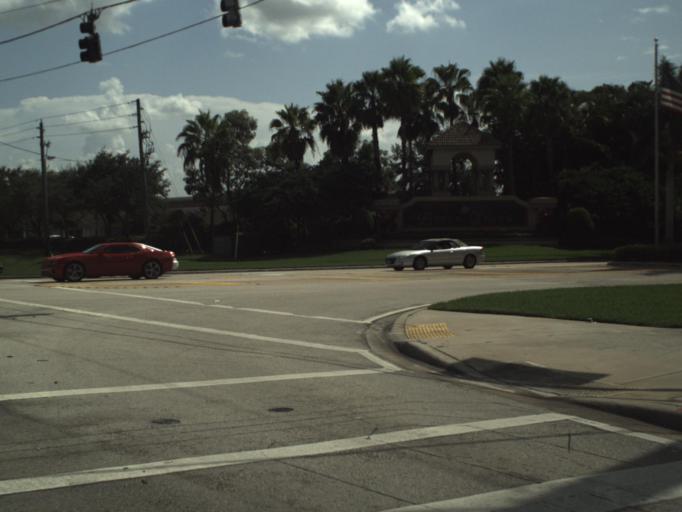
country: US
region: Florida
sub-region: Palm Beach County
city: Royal Palm Beach
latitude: 26.6883
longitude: -80.2020
